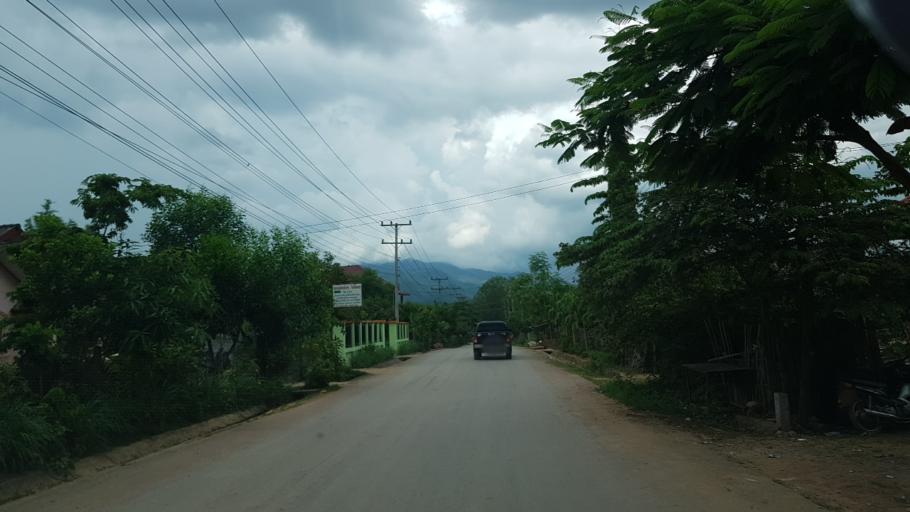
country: LA
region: Oudomxai
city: Muang Xay
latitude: 20.6707
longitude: 101.9664
